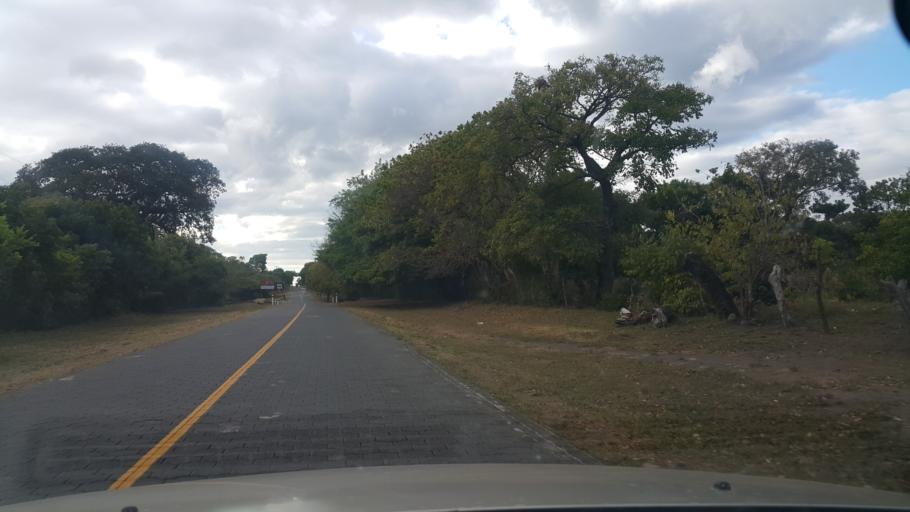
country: NI
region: Rivas
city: Moyogalpa
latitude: 11.4933
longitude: -85.6722
